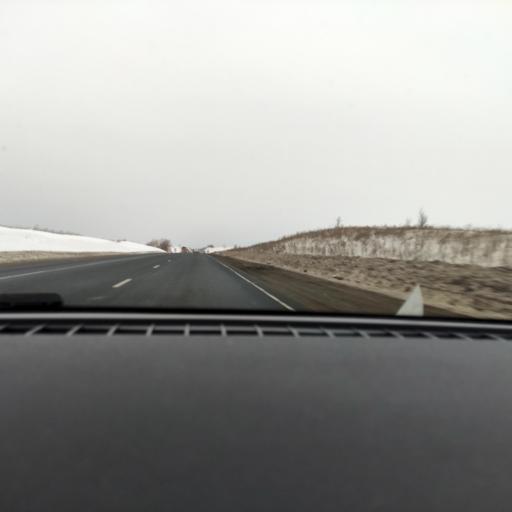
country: RU
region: Samara
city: Novosemeykino
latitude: 53.4022
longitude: 50.3964
